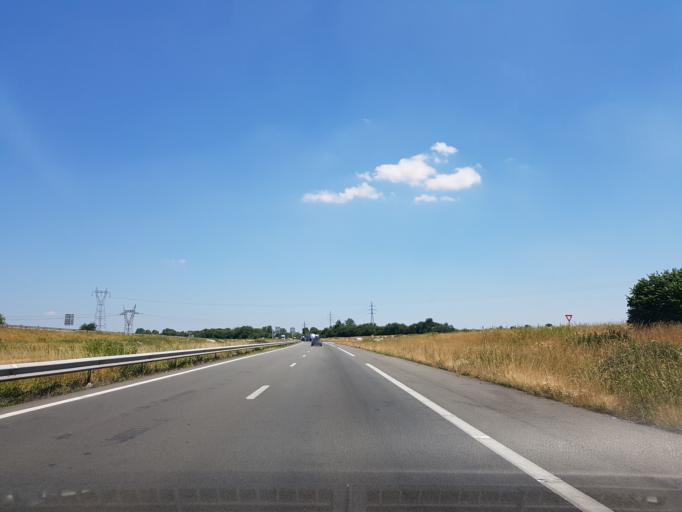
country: FR
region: Nord-Pas-de-Calais
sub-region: Departement du Nord
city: Hordain
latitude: 50.2542
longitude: 3.3223
